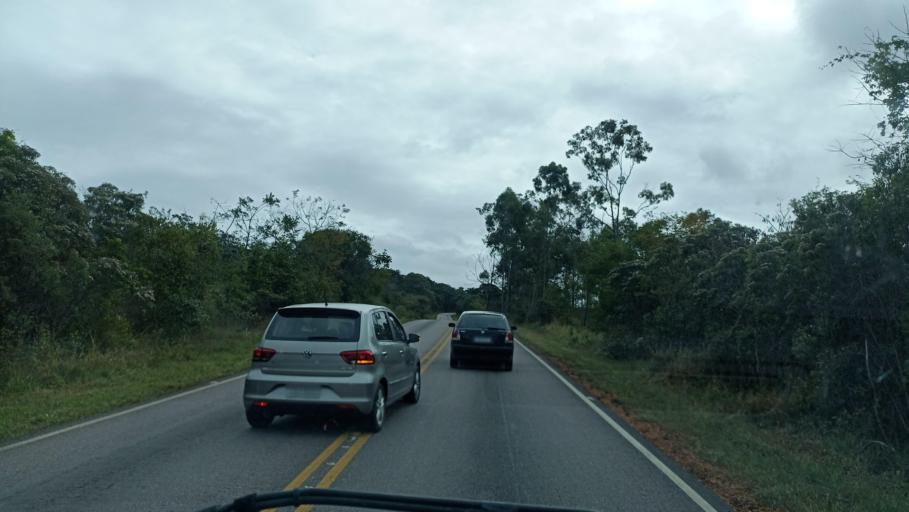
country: BR
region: Bahia
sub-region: Andarai
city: Vera Cruz
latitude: -12.9300
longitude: -41.2469
